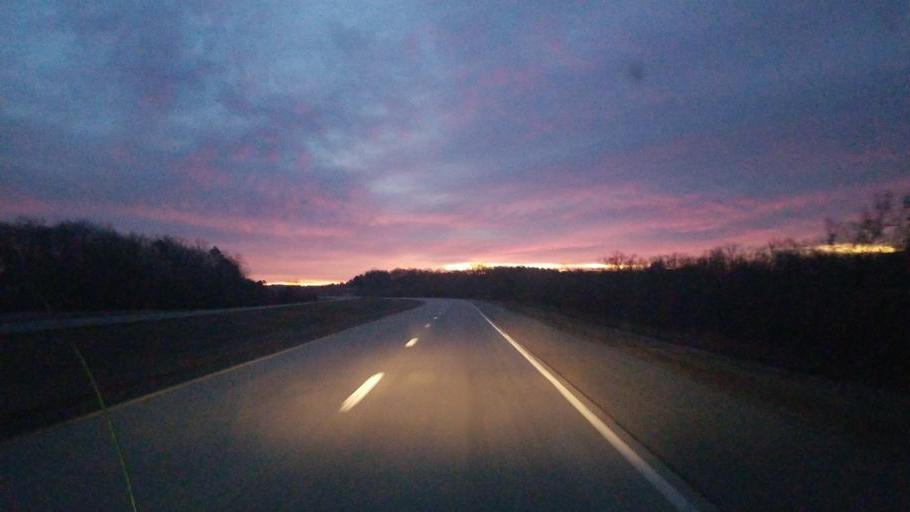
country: US
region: Missouri
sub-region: Shannon County
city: Winona
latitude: 36.9971
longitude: -91.4570
